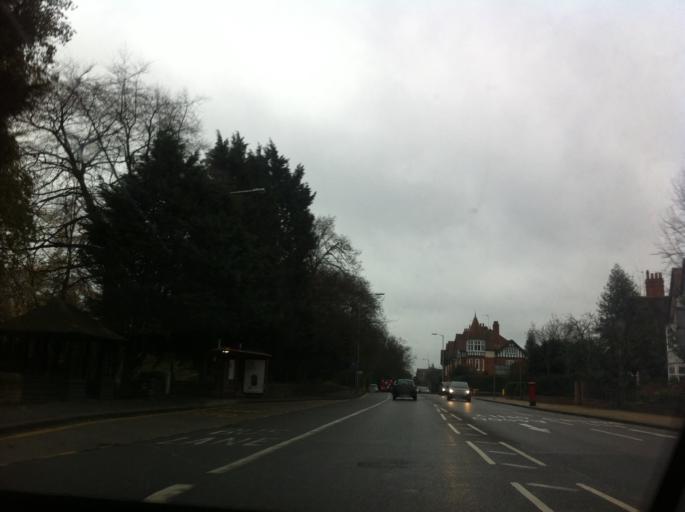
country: GB
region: England
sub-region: Northamptonshire
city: Earls Barton
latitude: 52.2645
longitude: -0.7507
